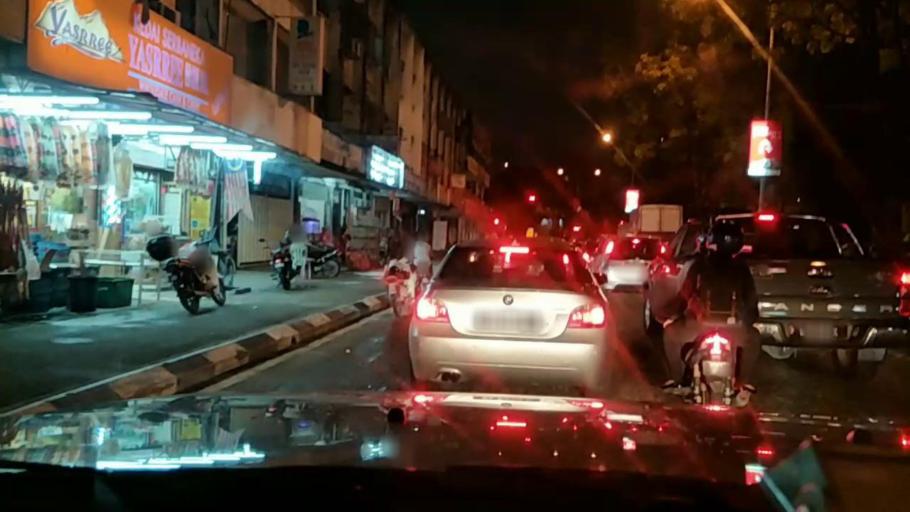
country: MY
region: Kuala Lumpur
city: Kuala Lumpur
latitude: 3.1337
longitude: 101.7182
